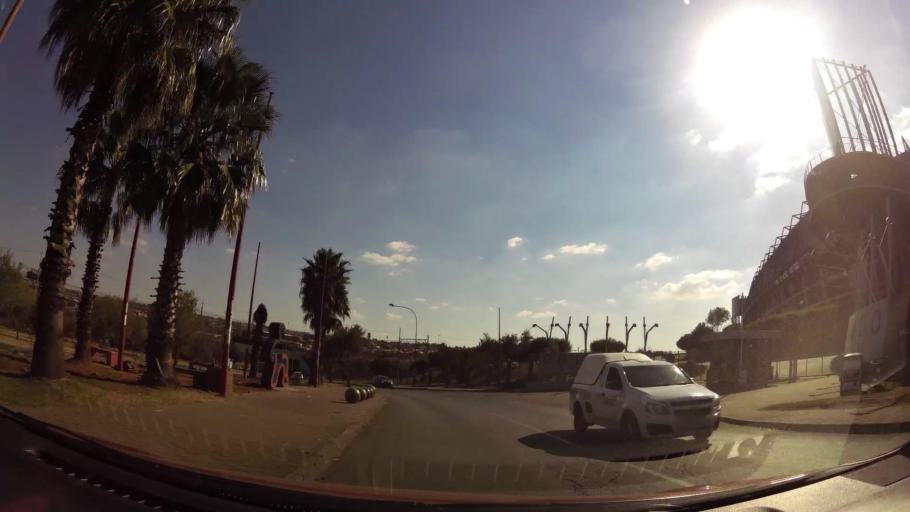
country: ZA
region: Gauteng
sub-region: City of Johannesburg Metropolitan Municipality
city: Soweto
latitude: -26.2328
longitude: 27.9215
